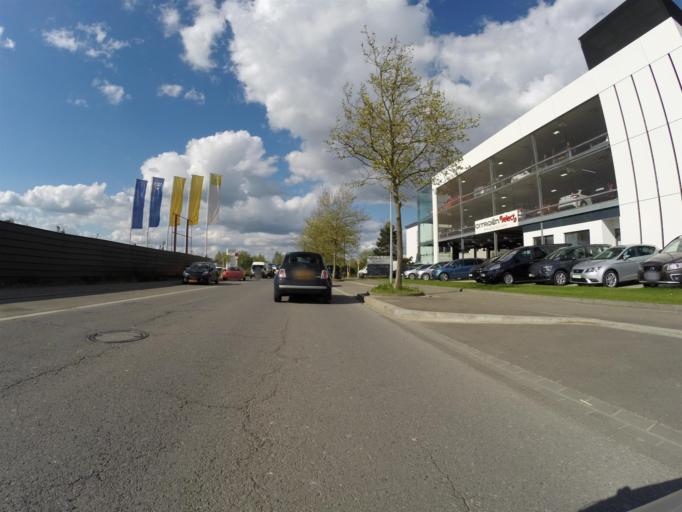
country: LU
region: Luxembourg
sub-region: Canton de Luxembourg
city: Luxembourg
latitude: 49.5840
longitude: 6.1186
